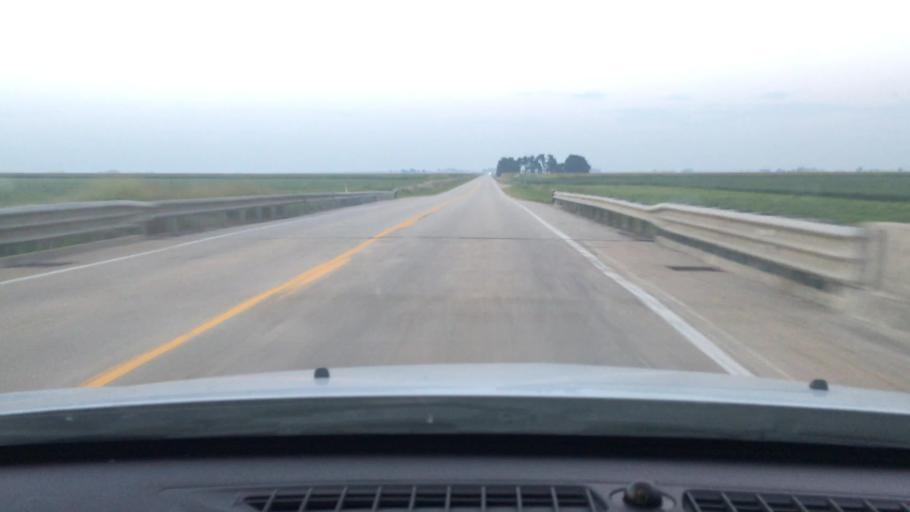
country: US
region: Illinois
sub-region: Ogle County
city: Rochelle
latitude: 41.8718
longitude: -89.0731
